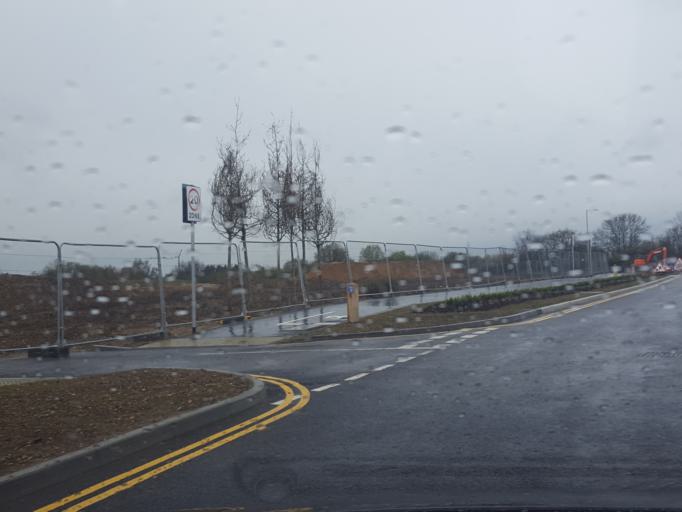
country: GB
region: England
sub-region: Essex
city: Great Horkesley
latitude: 51.9182
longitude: 0.8875
